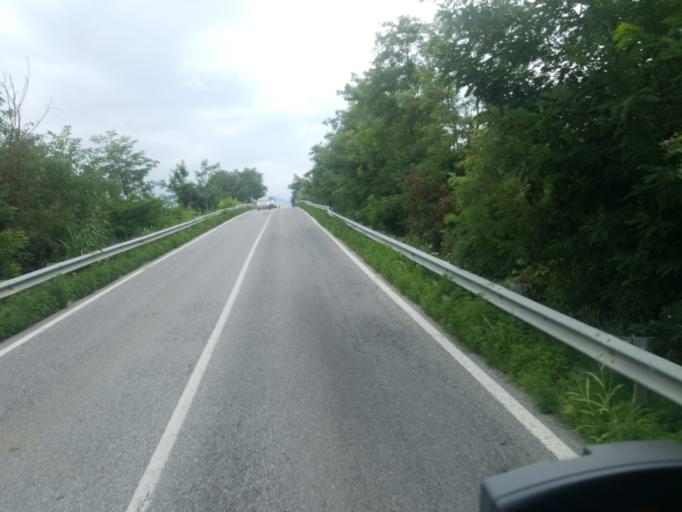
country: IT
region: Piedmont
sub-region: Provincia di Cuneo
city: Briaglia
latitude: 44.4270
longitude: 7.8559
